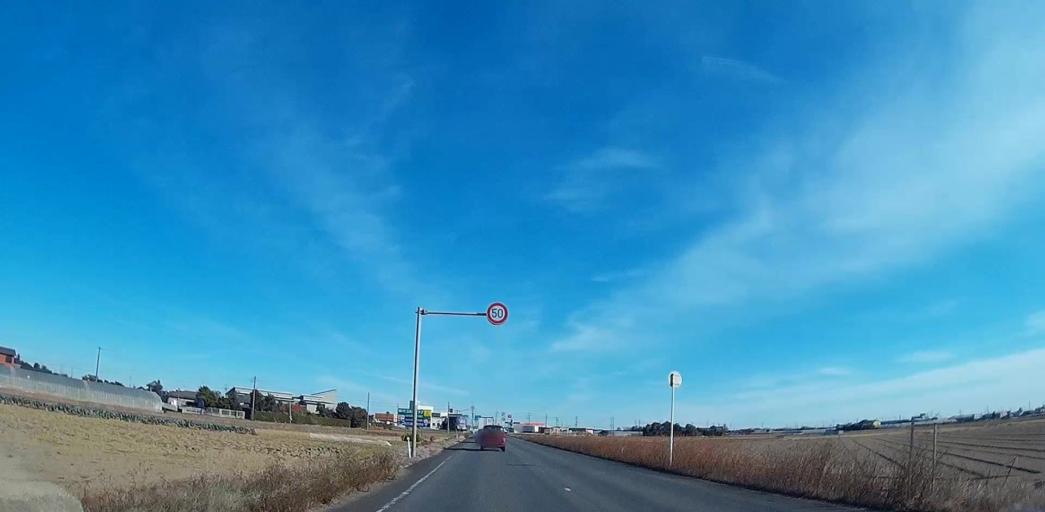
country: JP
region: Chiba
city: Yokaichiba
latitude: 35.7402
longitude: 140.5932
